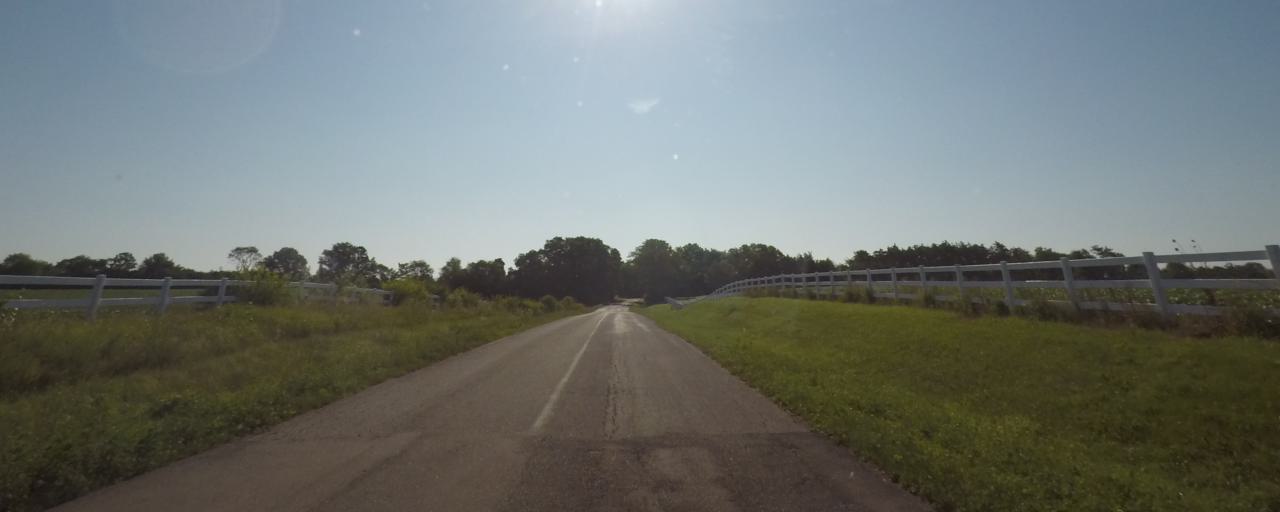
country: US
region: Wisconsin
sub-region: Jefferson County
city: Palmyra
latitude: 42.9190
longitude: -88.5497
